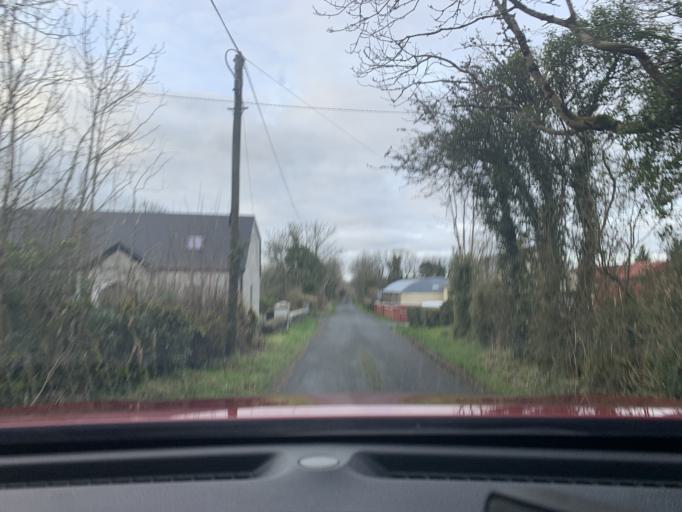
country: IE
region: Connaught
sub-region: Sligo
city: Ballymote
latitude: 54.0046
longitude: -8.5745
